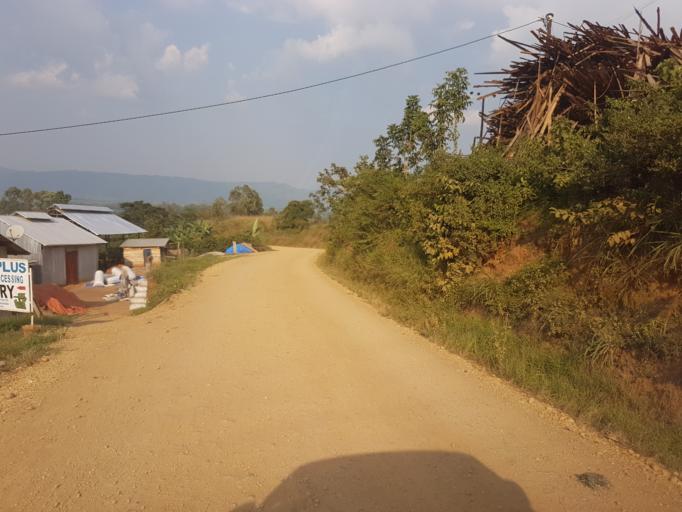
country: UG
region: Western Region
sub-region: Rukungiri District
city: Rukungiri
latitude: -0.6467
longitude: 29.8432
